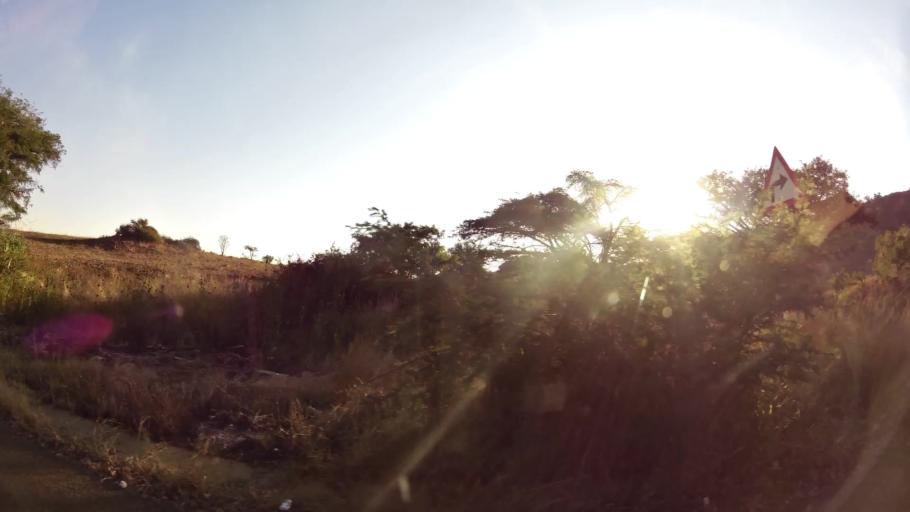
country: ZA
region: Gauteng
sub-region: City of Tshwane Metropolitan Municipality
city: Pretoria
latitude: -25.7320
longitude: 28.1163
